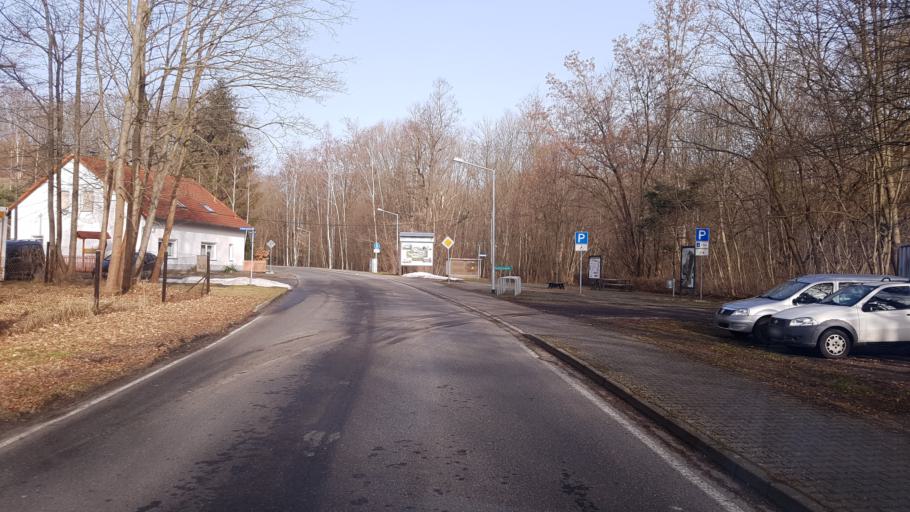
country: DE
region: Brandenburg
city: Schipkau
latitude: 51.5215
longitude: 13.8355
